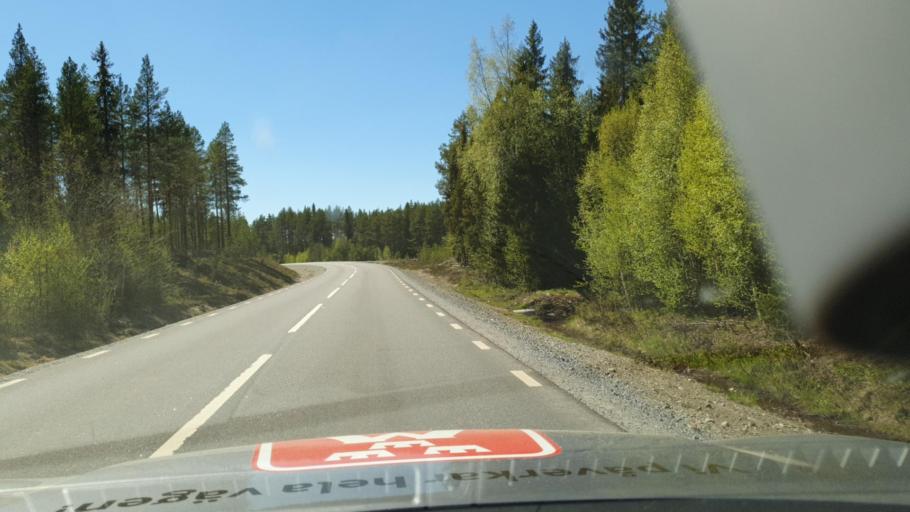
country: SE
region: Vaesternorrland
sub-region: OErnskoeldsviks Kommun
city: Bredbyn
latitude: 63.8807
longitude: 18.5126
